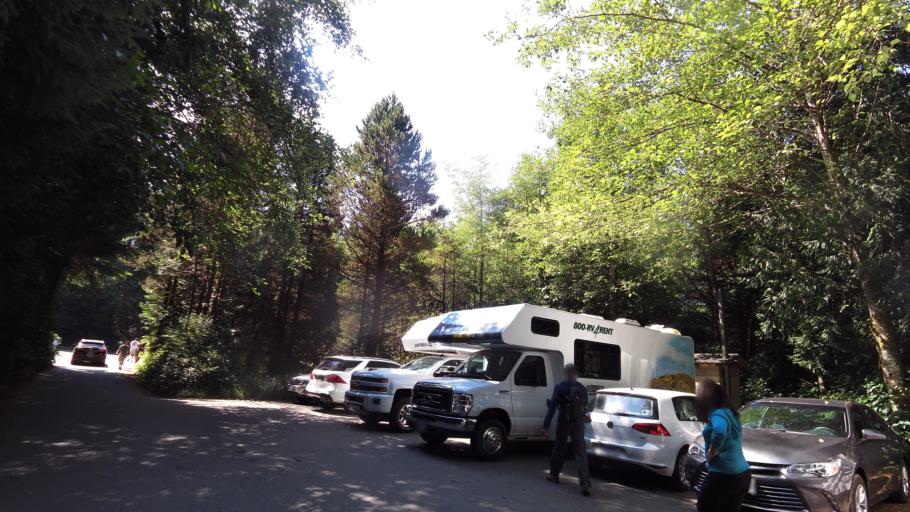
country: CA
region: British Columbia
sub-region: Regional District of Alberni-Clayoquot
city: Ucluelet
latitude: 49.0419
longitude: -125.6813
